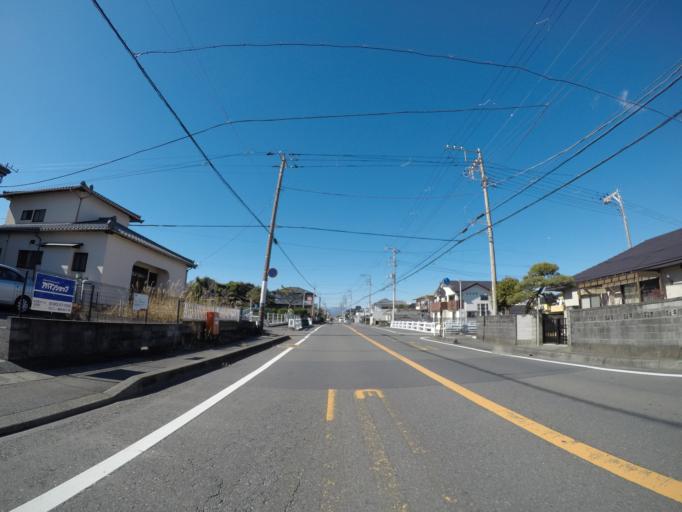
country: JP
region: Shizuoka
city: Numazu
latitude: 35.1288
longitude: 138.7861
